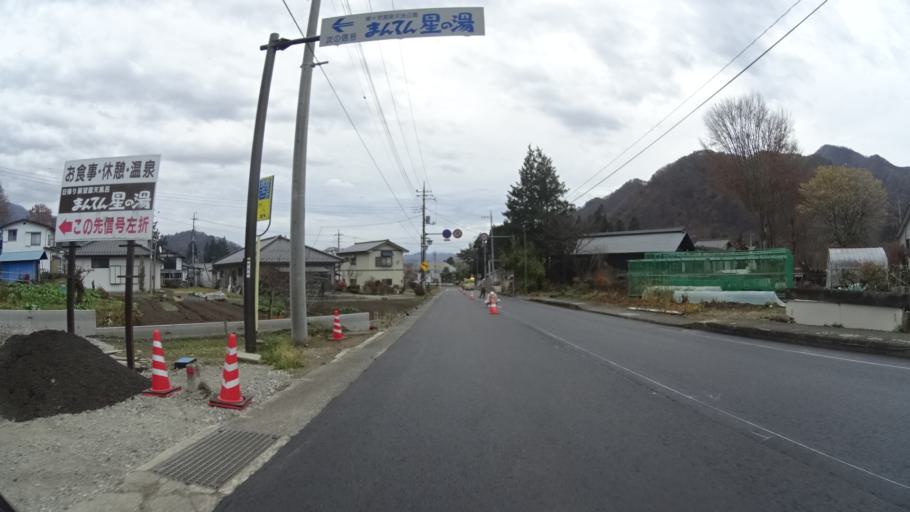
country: JP
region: Gunma
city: Nakanojomachi
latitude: 36.7267
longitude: 138.8838
